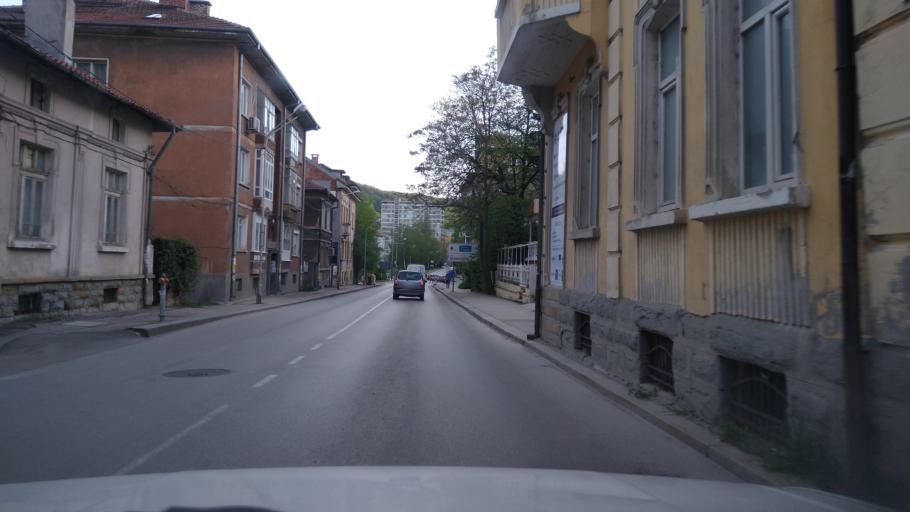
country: BG
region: Gabrovo
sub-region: Obshtina Gabrovo
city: Gabrovo
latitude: 42.8742
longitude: 25.3163
